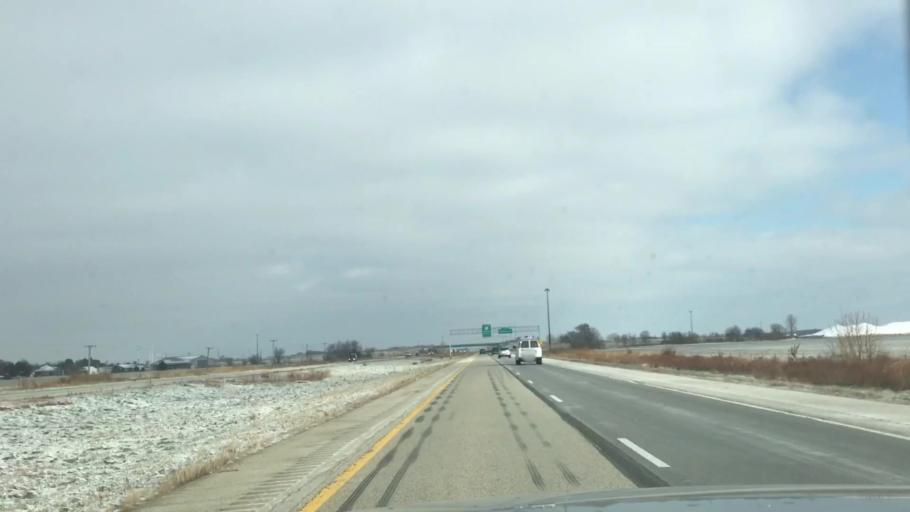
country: US
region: Illinois
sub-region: Sangamon County
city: Divernon
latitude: 39.5605
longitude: -89.6460
